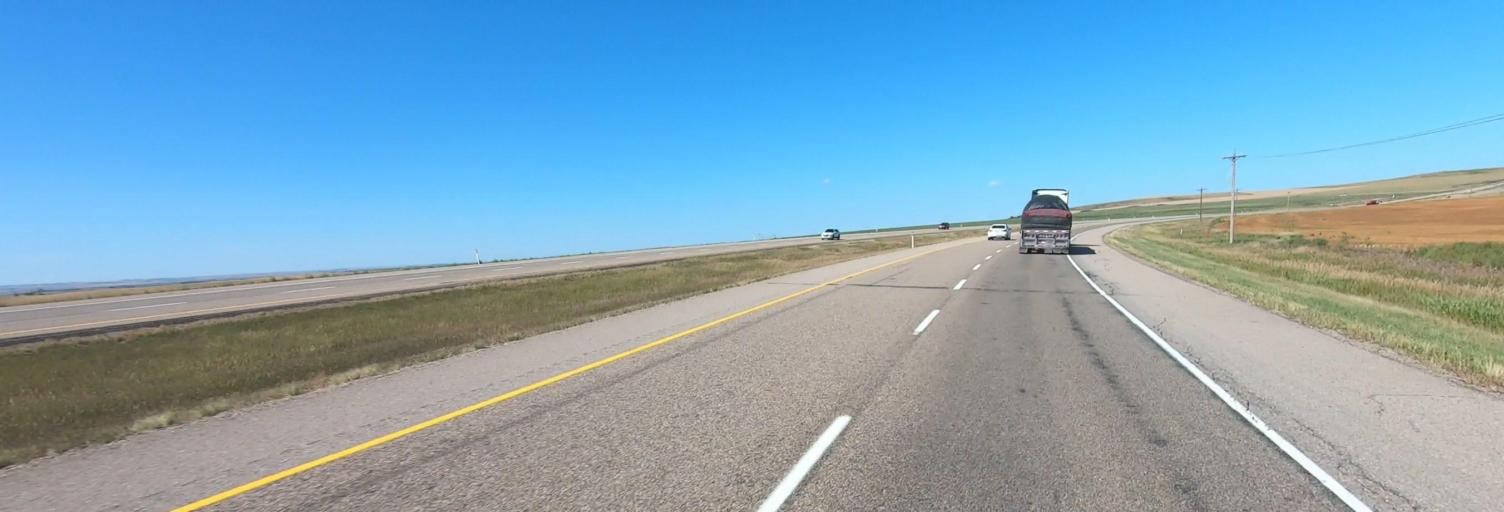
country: CA
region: Alberta
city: Bassano
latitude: 50.8347
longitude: -112.8100
